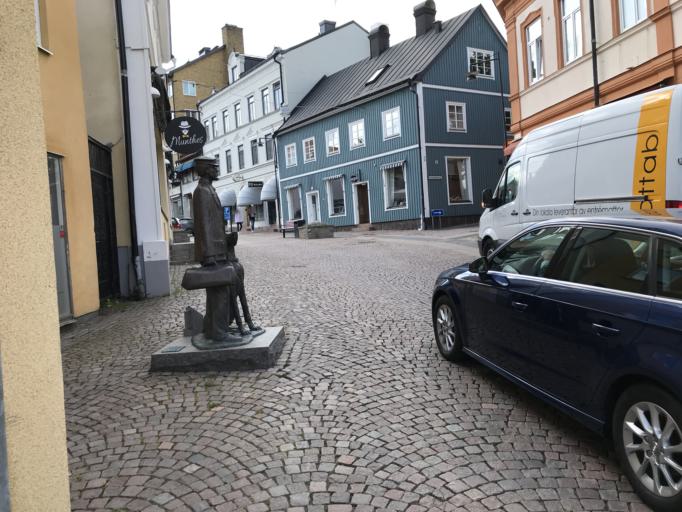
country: SE
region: Kalmar
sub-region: Oskarshamns Kommun
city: Oskarshamn
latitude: 57.2669
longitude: 16.4483
